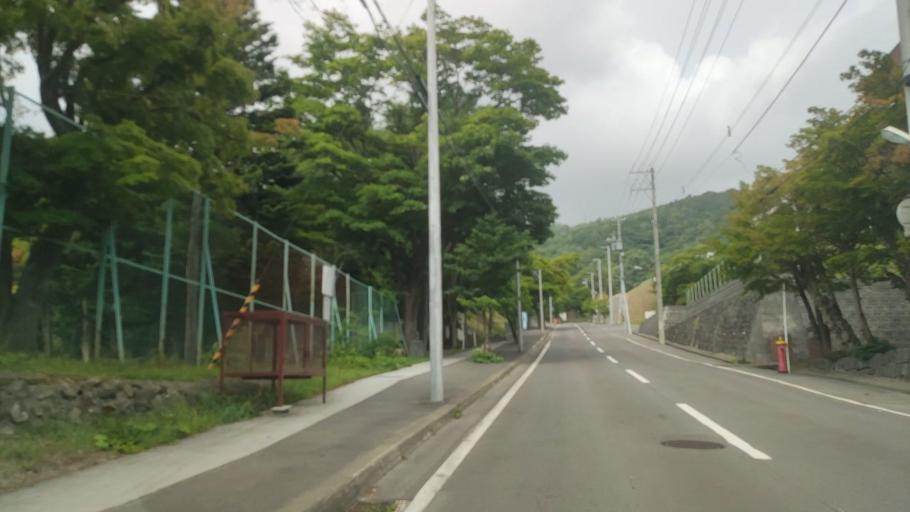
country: JP
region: Hokkaido
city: Otaru
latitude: 43.1915
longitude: 140.9815
